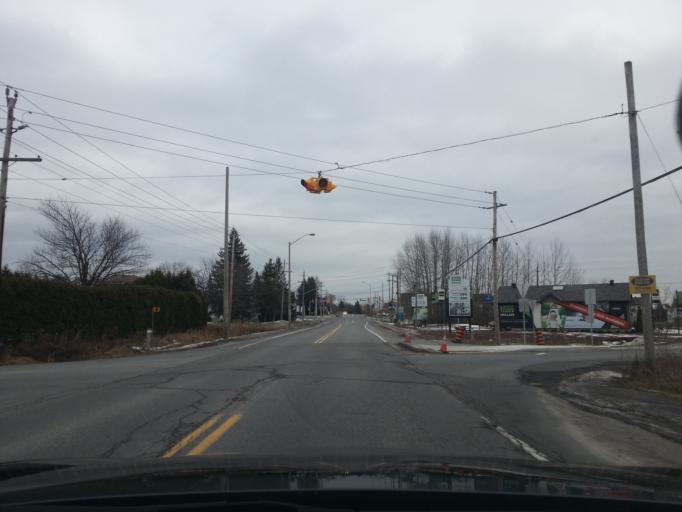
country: CA
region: Ontario
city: Ottawa
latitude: 45.4306
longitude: -75.5179
